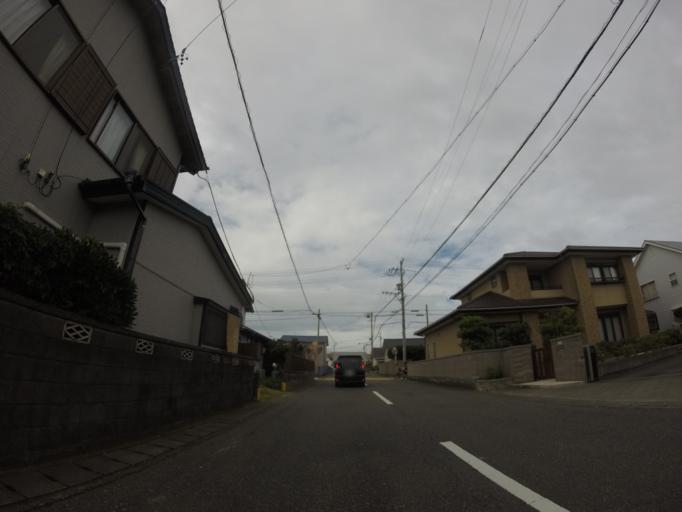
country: JP
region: Shizuoka
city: Oyama
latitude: 34.5992
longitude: 138.2221
